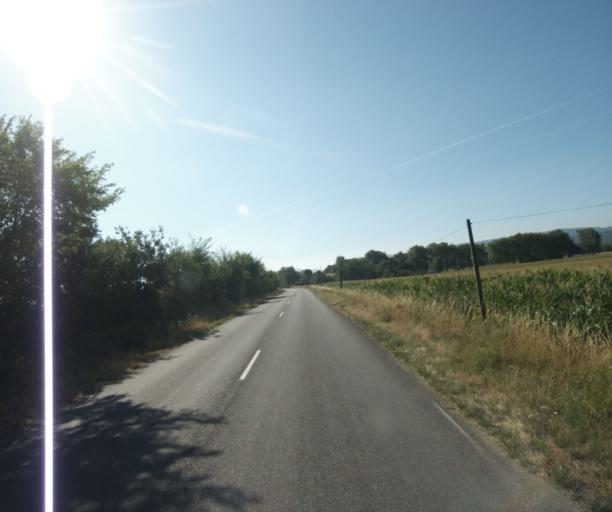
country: FR
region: Midi-Pyrenees
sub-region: Departement de la Haute-Garonne
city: Revel
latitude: 43.4750
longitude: 2.0180
